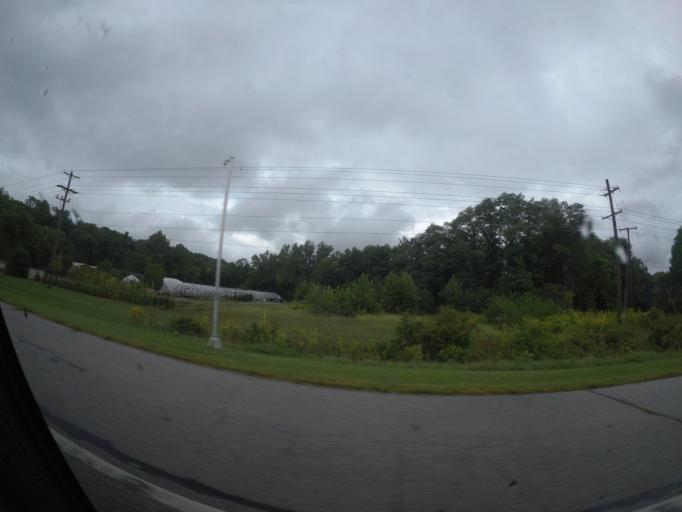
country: US
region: Indiana
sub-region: Montgomery County
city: Crawfordsville
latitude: 40.0528
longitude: -86.9037
